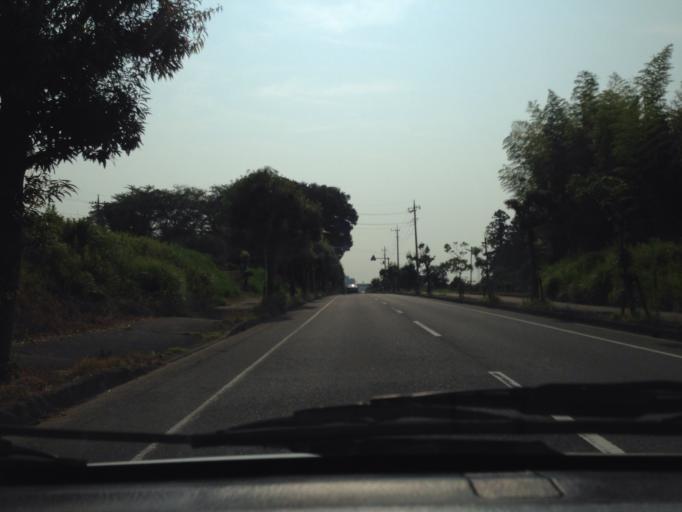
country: JP
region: Ibaraki
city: Ami
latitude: 36.0586
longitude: 140.2090
